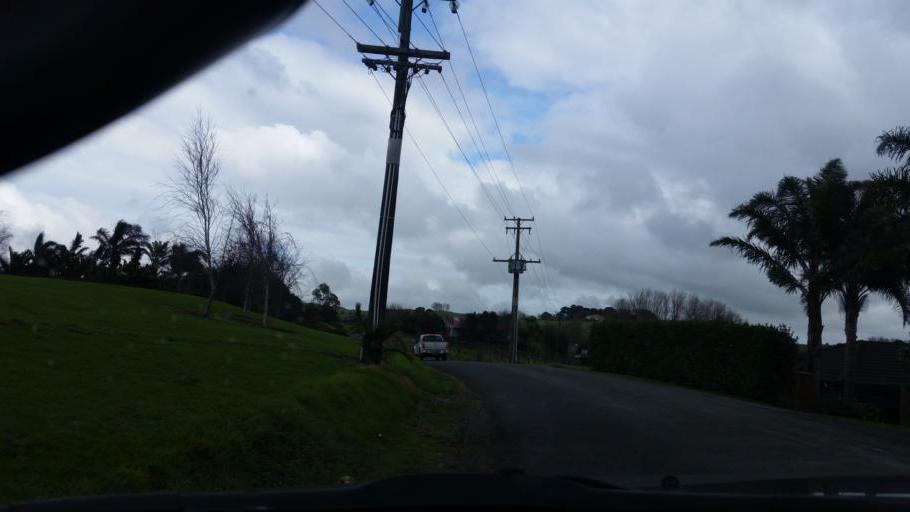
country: NZ
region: Northland
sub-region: Whangarei
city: Ruakaka
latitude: -36.1177
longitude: 174.3489
